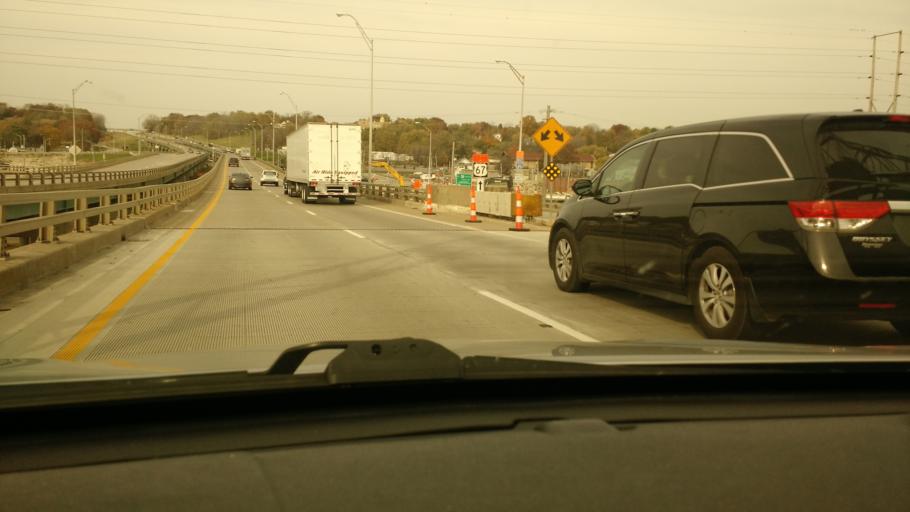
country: US
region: Iowa
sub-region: Scott County
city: Bettendorf
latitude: 41.5235
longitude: -90.5132
